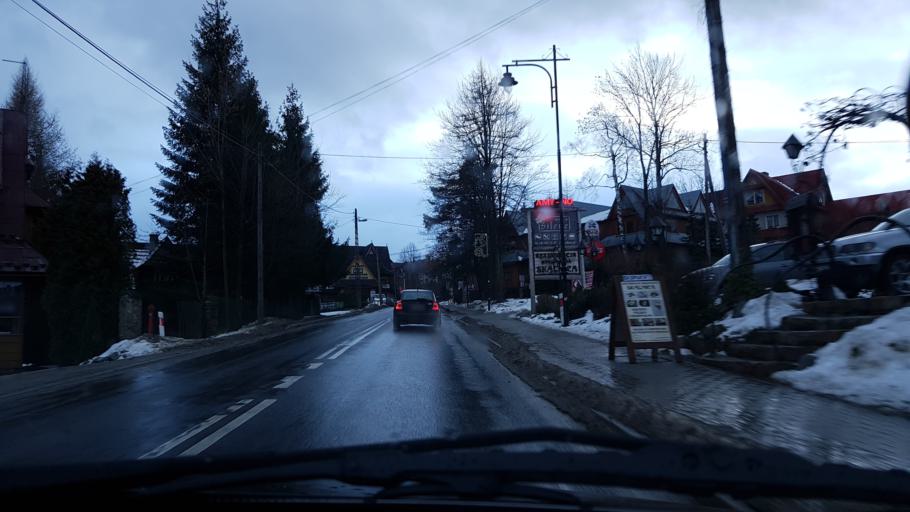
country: PL
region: Lesser Poland Voivodeship
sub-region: Powiat tatrzanski
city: Bukowina Tatrzanska
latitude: 49.3338
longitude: 20.0977
